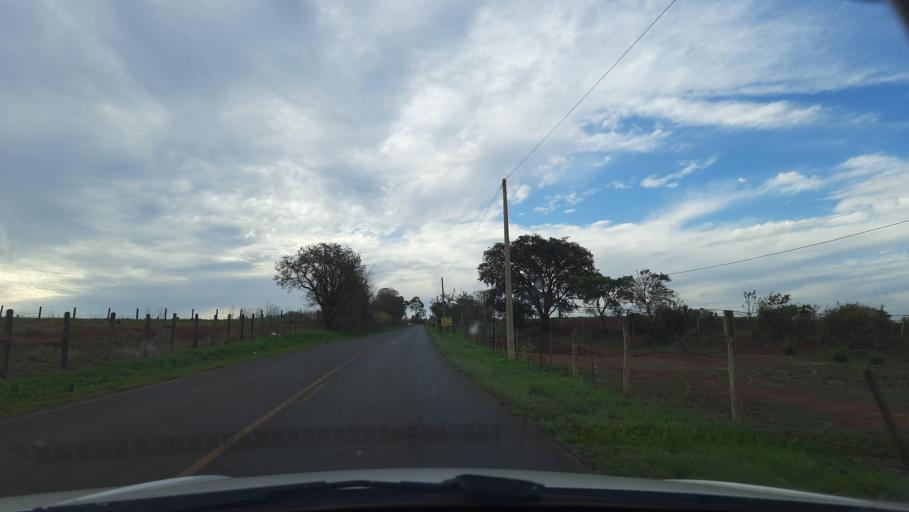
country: BR
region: Sao Paulo
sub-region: Casa Branca
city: Casa Branca
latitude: -21.7635
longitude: -47.1051
